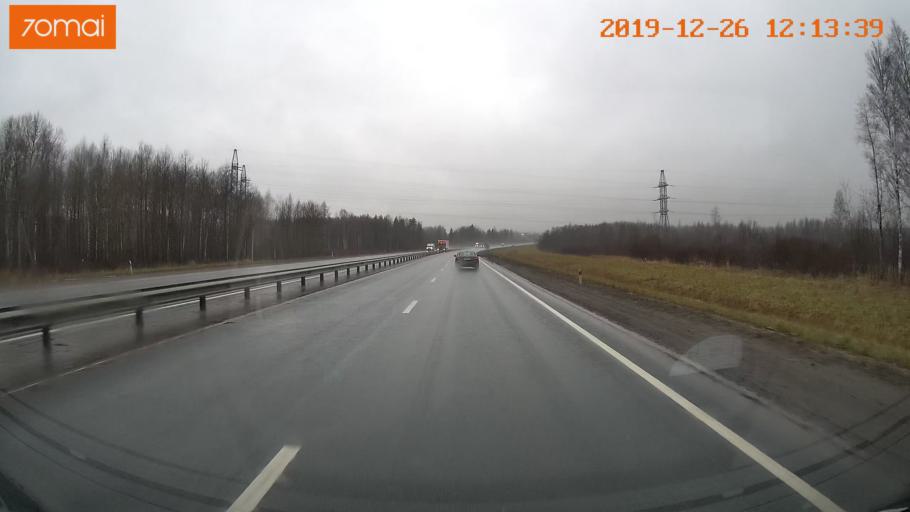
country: RU
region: Vologda
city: Tonshalovo
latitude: 59.2189
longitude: 37.9533
